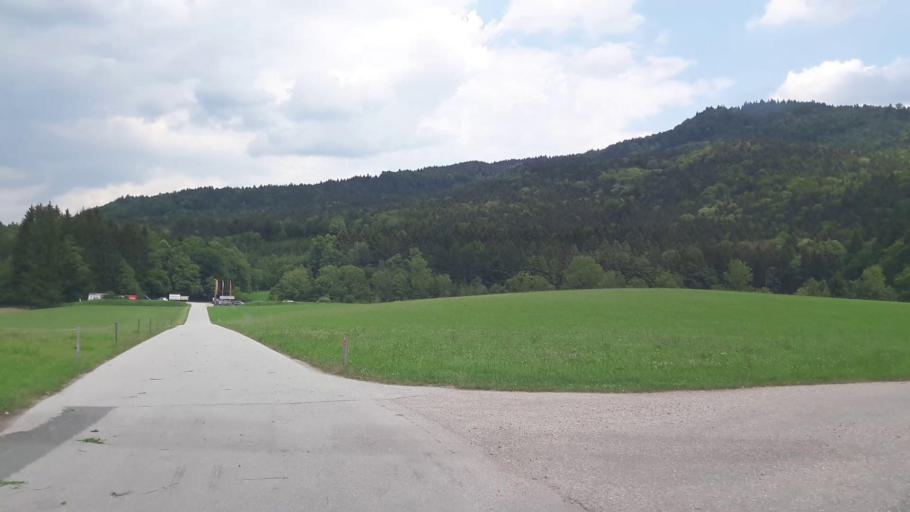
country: AT
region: Salzburg
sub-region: Politischer Bezirk Salzburg-Umgebung
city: Henndorf am Wallersee
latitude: 47.8902
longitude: 13.2146
